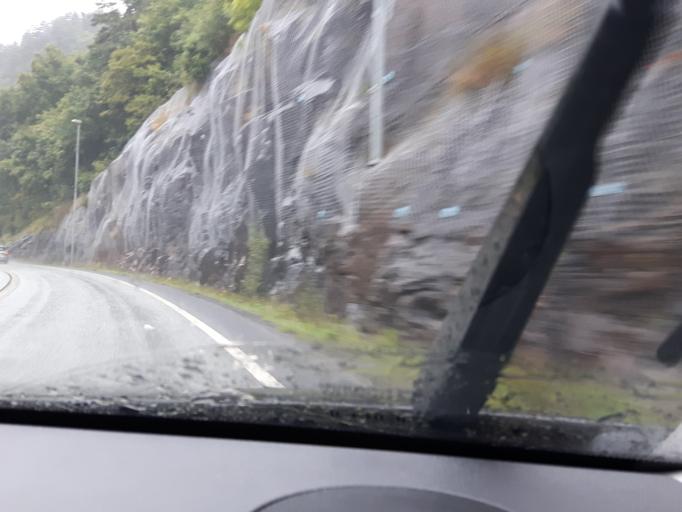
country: NO
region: Vest-Agder
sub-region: Mandal
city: Mandal
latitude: 58.0465
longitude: 7.4172
